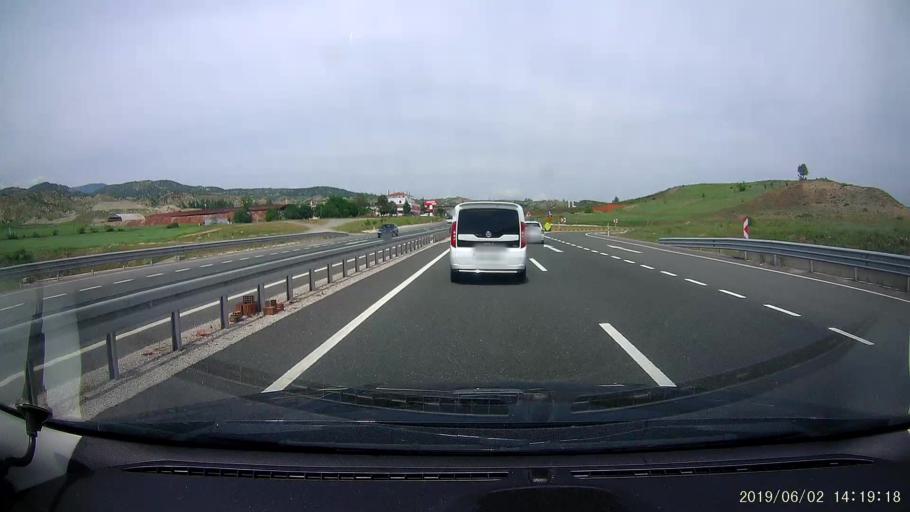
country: TR
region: Kastamonu
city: Tosya
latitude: 40.9634
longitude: 33.9738
